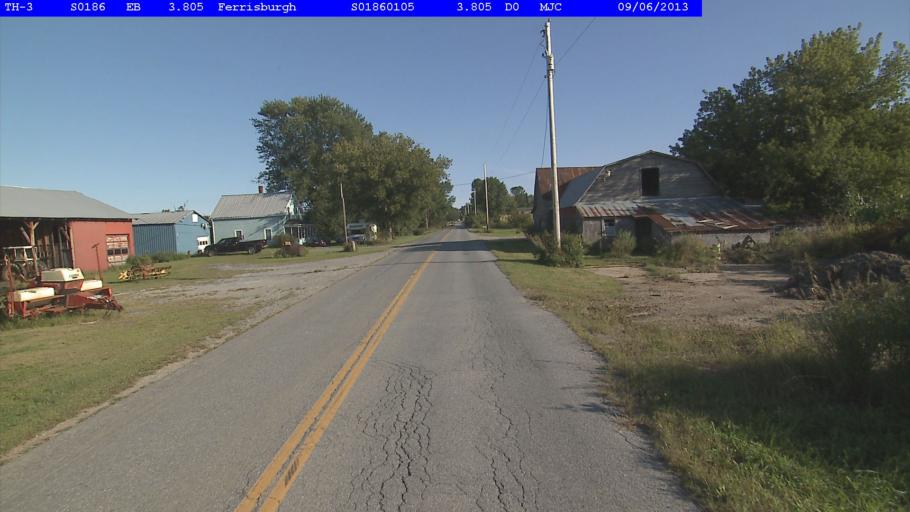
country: US
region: Vermont
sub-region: Addison County
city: Vergennes
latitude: 44.1728
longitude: -73.3037
